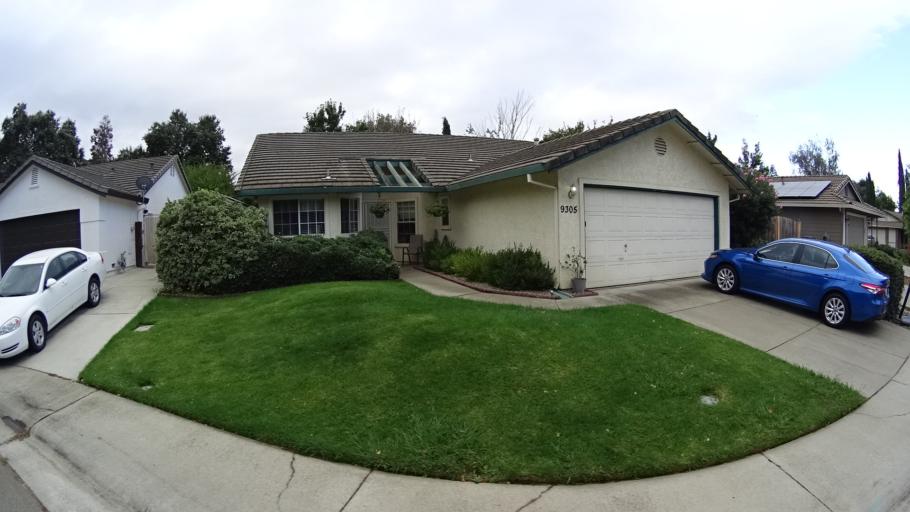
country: US
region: California
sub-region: Sacramento County
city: Laguna
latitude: 38.4197
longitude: -121.4184
